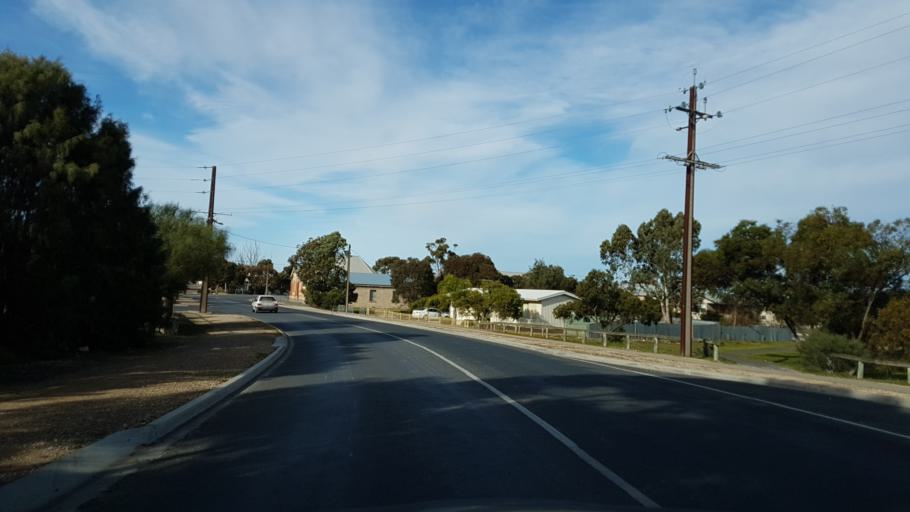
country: AU
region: South Australia
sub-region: Murray Bridge
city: Tailem Bend
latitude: -35.2501
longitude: 139.4552
